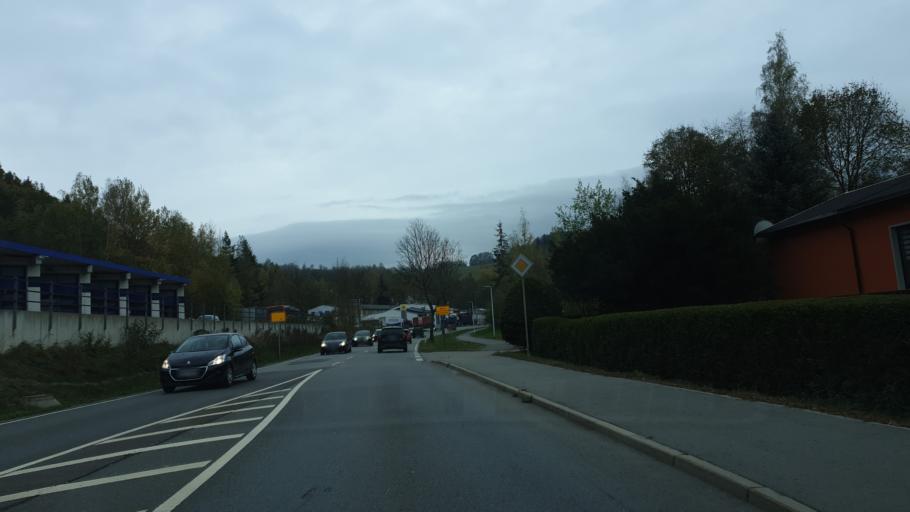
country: DE
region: Saxony
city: Schwarzenberg
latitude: 50.5255
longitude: 12.7892
